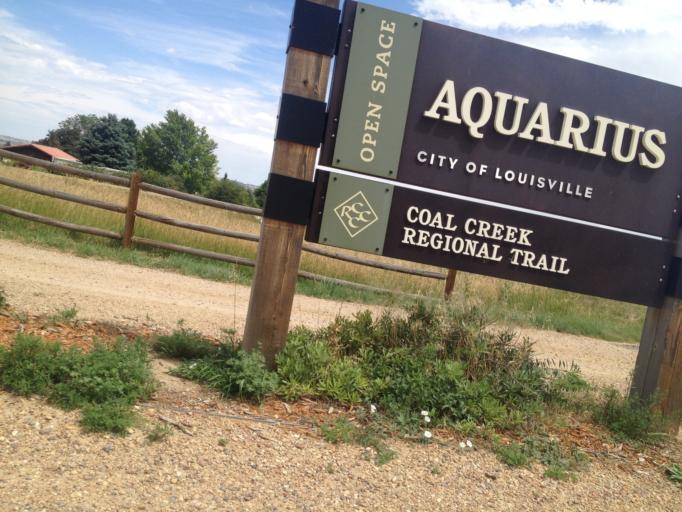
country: US
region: Colorado
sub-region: Boulder County
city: Louisville
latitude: 39.9728
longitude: -105.1152
